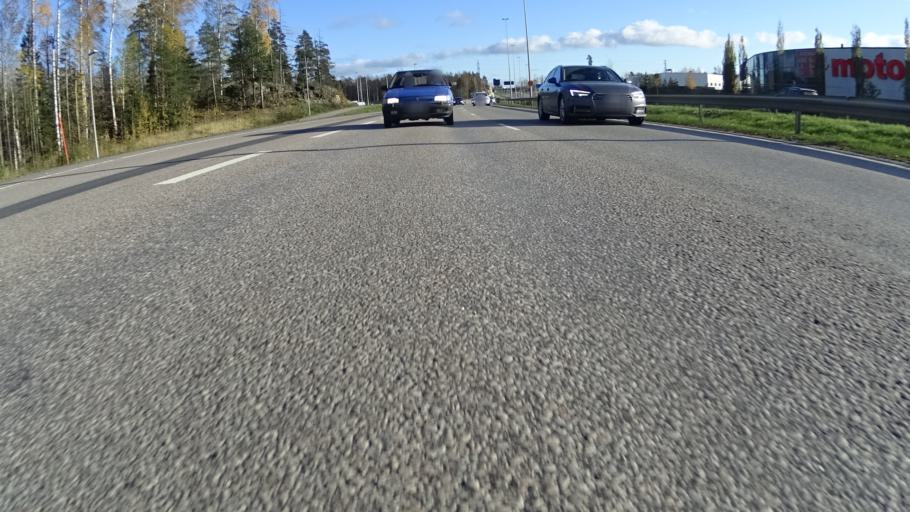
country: FI
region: Uusimaa
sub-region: Helsinki
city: Vantaa
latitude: 60.2973
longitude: 24.9280
